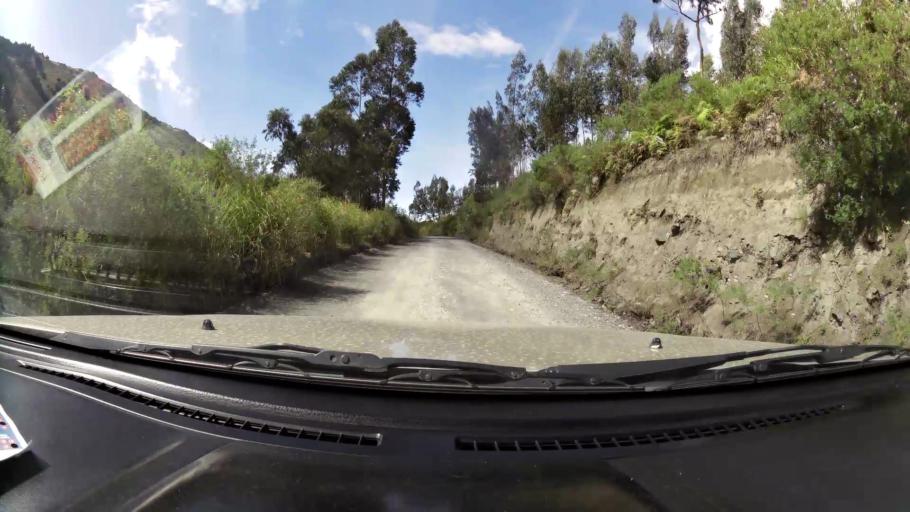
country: EC
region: Tungurahua
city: Banos
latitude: -1.4861
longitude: -78.5118
